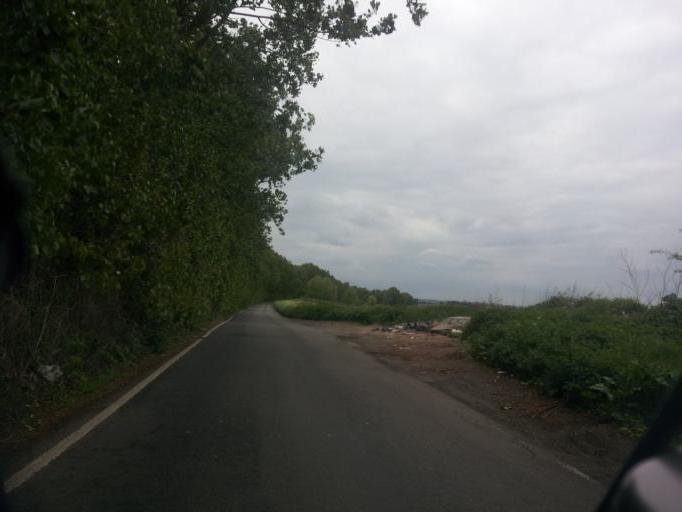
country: GB
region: England
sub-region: Kent
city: Queenborough
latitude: 51.3844
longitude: 0.7155
